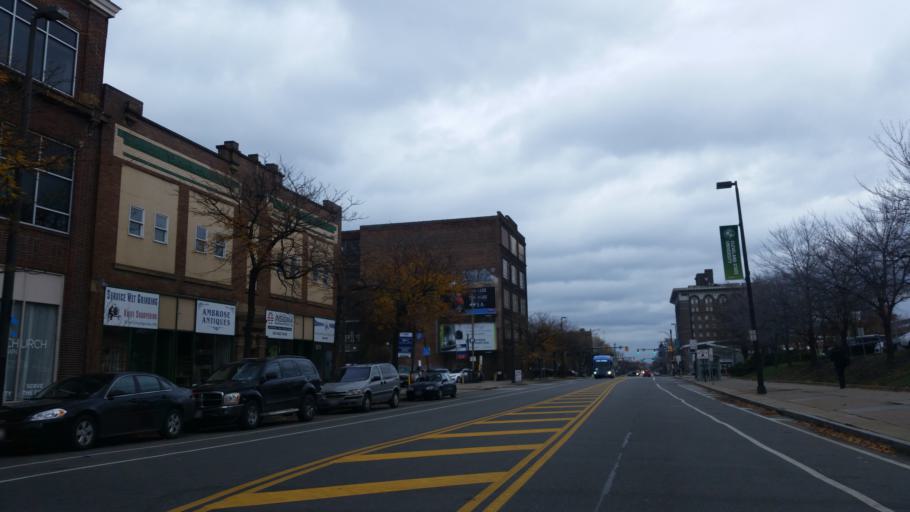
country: US
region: Ohio
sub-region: Cuyahoga County
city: Cleveland
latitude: 41.5000
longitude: -81.6776
